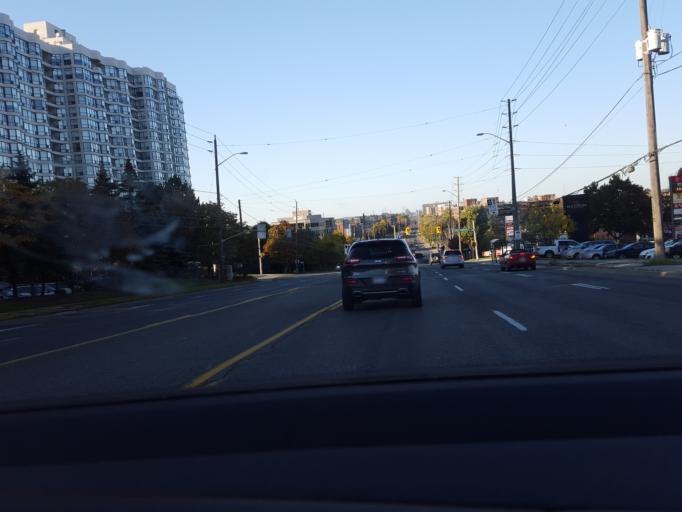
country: CA
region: Ontario
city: North York
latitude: 43.8045
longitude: -79.4217
